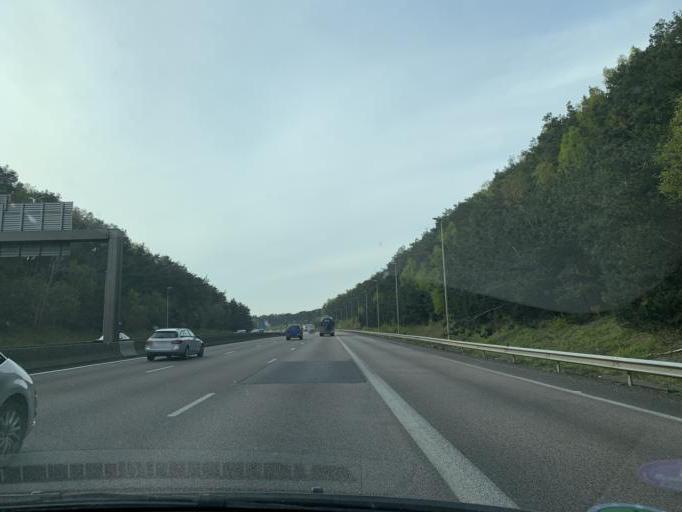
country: FR
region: Haute-Normandie
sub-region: Departement de la Seine-Maritime
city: Oissel
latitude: 49.3398
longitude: 1.0691
